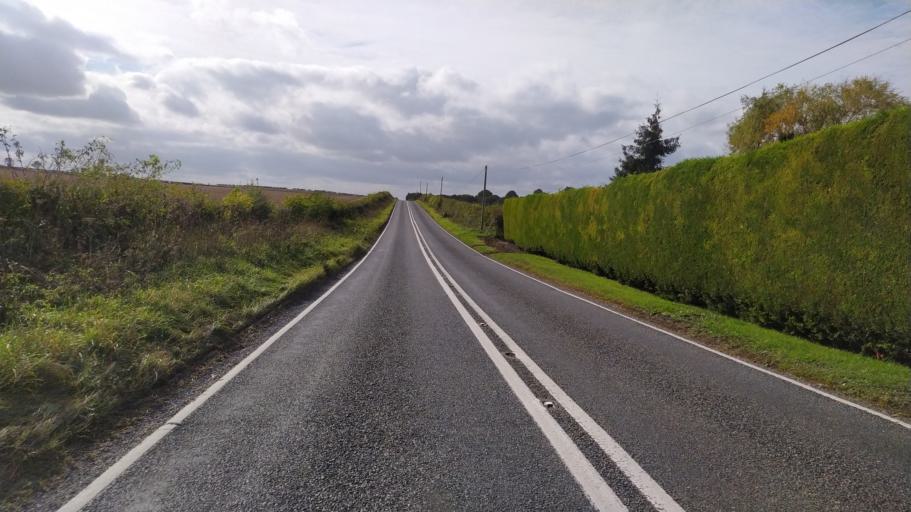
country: GB
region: England
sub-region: Hampshire
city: Kings Worthy
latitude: 51.1492
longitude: -1.3578
